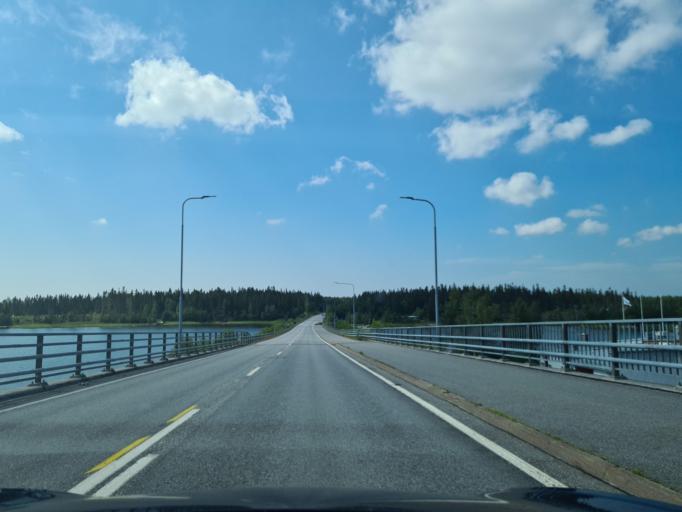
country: FI
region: Ostrobothnia
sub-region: Vaasa
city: Replot
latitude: 63.2068
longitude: 21.4630
